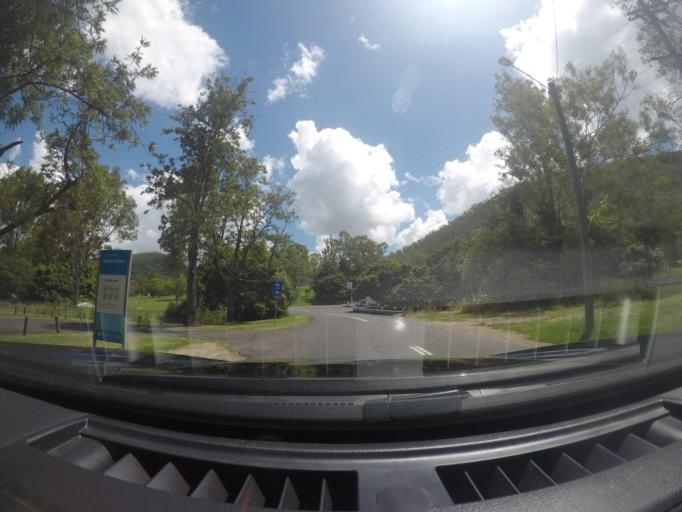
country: AU
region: Queensland
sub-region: Moreton Bay
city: Woodford
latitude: -27.1195
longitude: 152.5507
